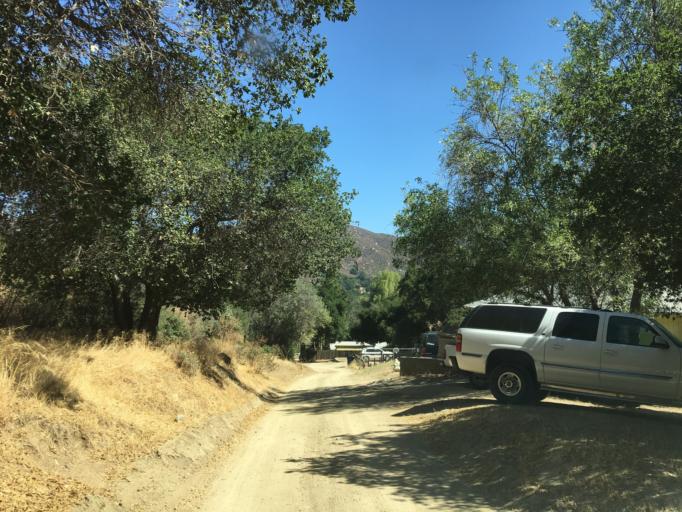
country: US
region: California
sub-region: Los Angeles County
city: Green Valley
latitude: 34.6099
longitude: -118.3969
